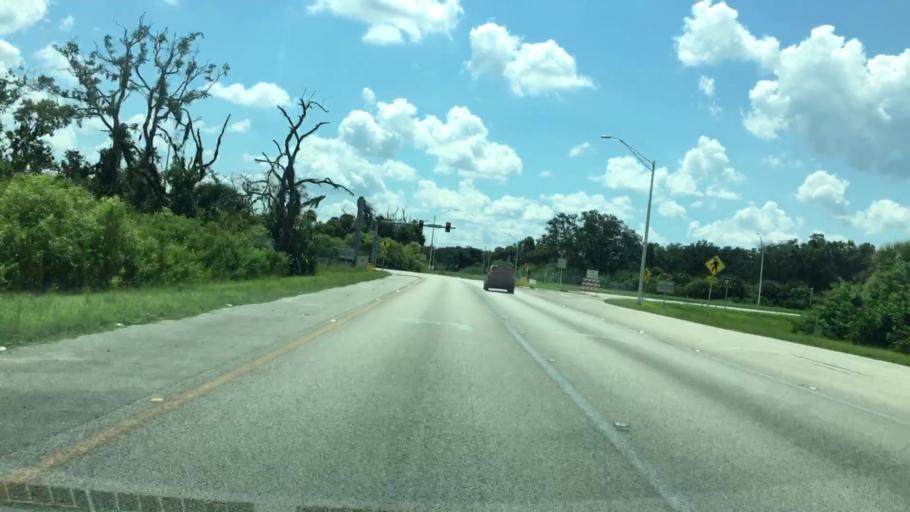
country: US
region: Florida
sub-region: Brevard County
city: South Patrick Shores
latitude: 28.1926
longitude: -80.7110
